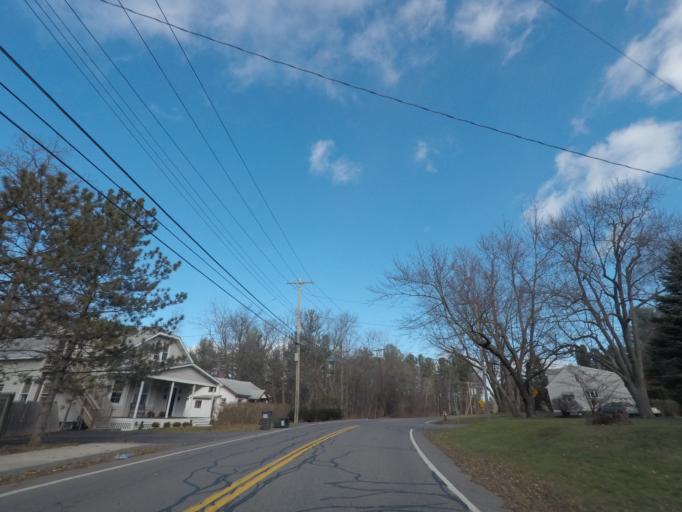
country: US
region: New York
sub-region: Schenectady County
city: Schenectady
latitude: 42.8112
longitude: -73.8914
